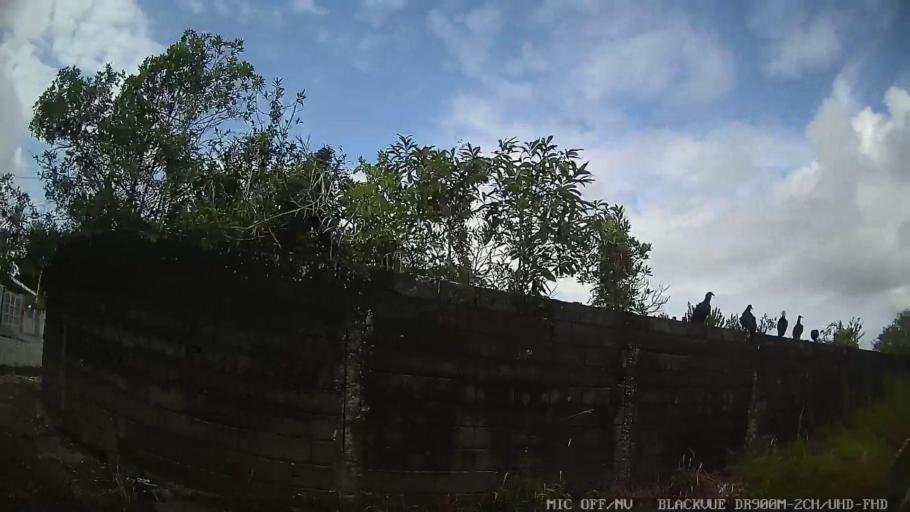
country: BR
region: Sao Paulo
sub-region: Itanhaem
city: Itanhaem
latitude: -24.1962
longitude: -46.8233
